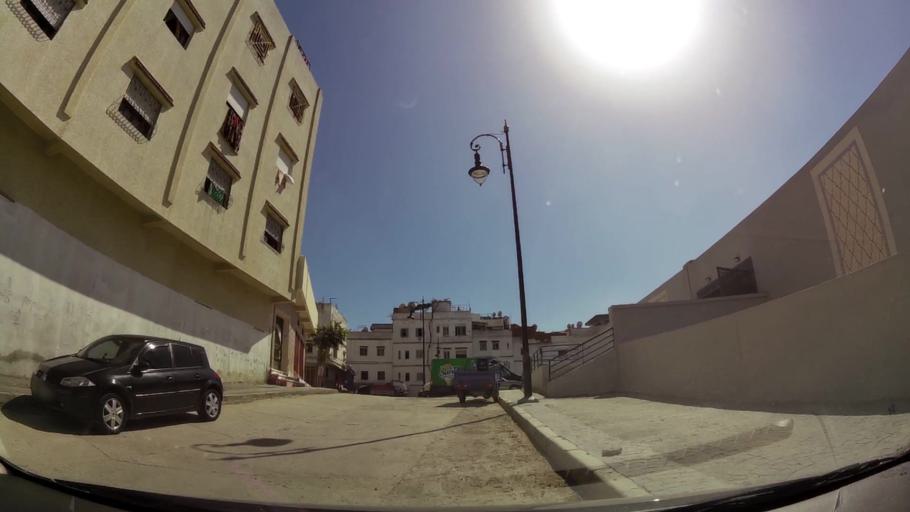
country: MA
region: Tanger-Tetouan
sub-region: Tanger-Assilah
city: Tangier
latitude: 35.7428
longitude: -5.8142
